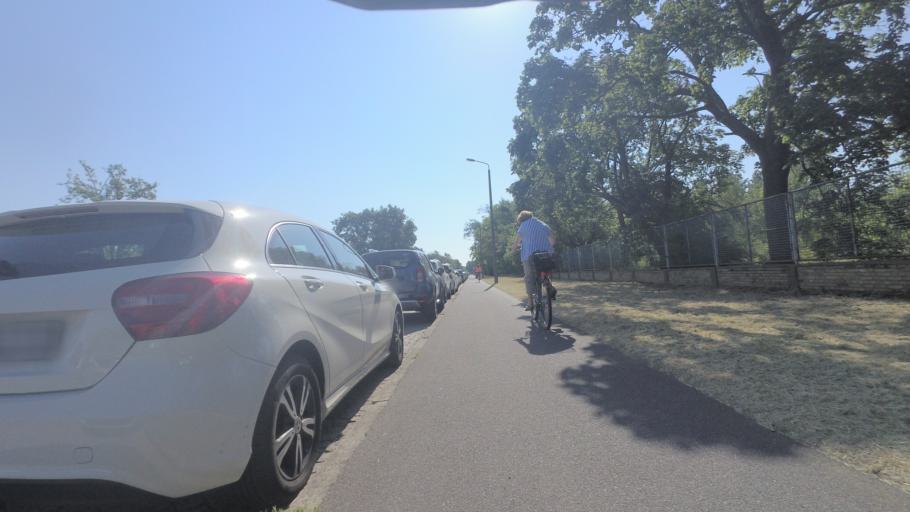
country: DE
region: Saxony-Anhalt
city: Dessau
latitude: 51.8371
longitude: 12.2038
